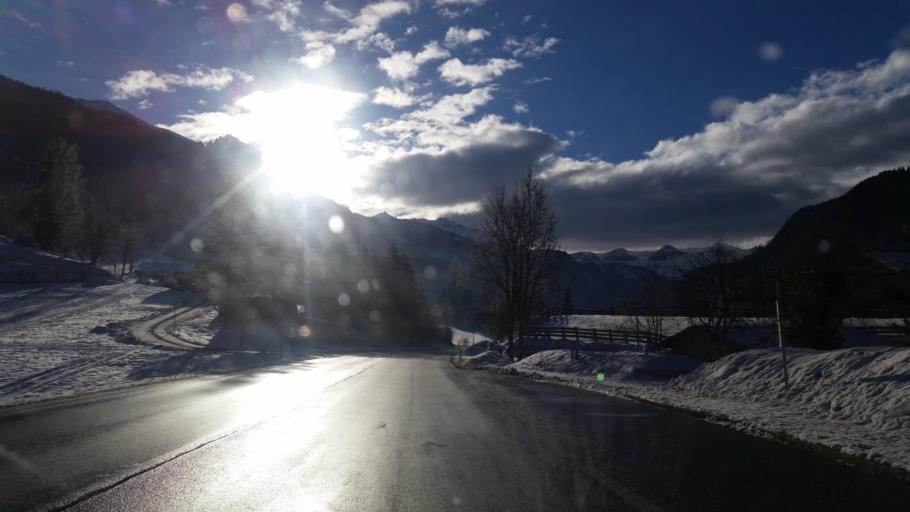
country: AT
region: Salzburg
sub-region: Politischer Bezirk Sankt Johann im Pongau
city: Forstau
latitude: 47.3427
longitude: 13.5038
